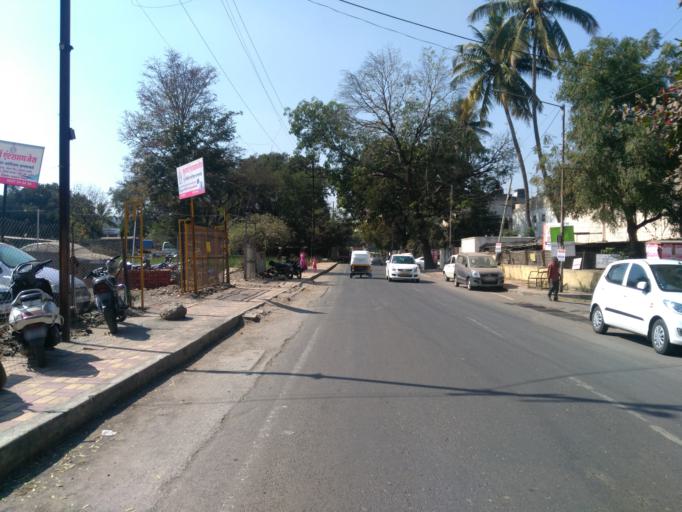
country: IN
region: Maharashtra
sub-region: Pune Division
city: Pune
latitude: 18.4786
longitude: 73.8589
